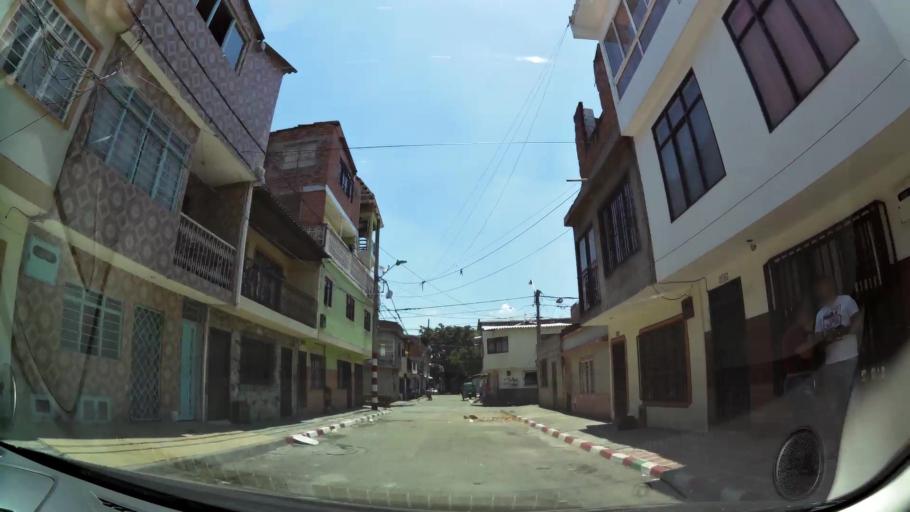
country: CO
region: Valle del Cauca
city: Cali
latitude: 3.4363
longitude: -76.5009
